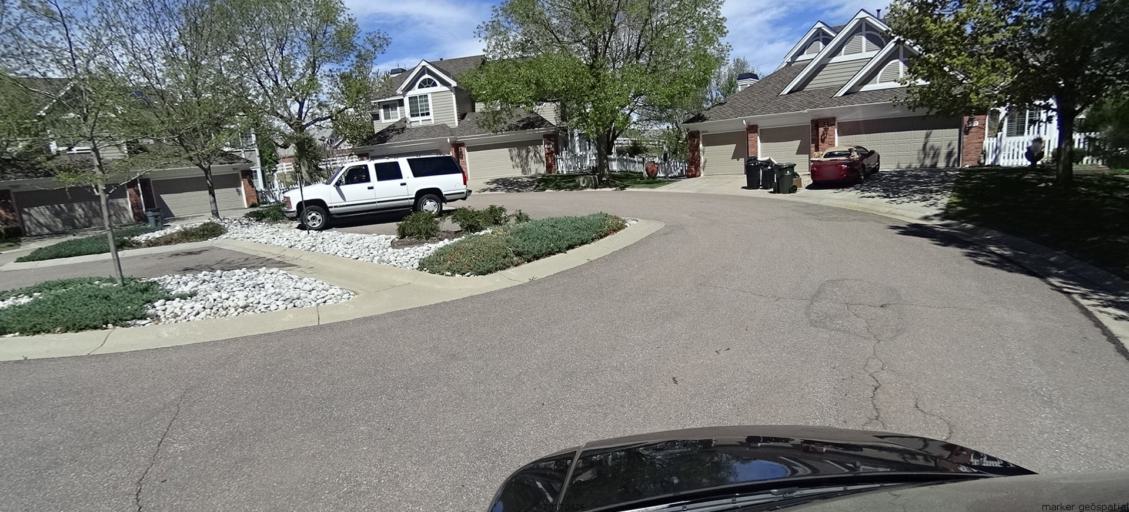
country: US
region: Colorado
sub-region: Douglas County
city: Carriage Club
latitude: 39.5370
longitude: -104.8905
